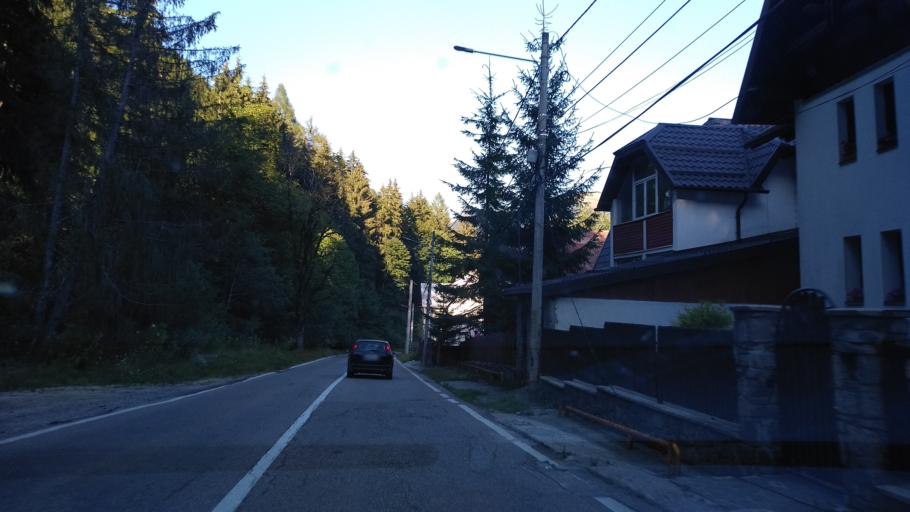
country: RO
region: Prahova
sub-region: Oras Sinaia
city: Sinaia
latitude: 45.3268
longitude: 25.5363
